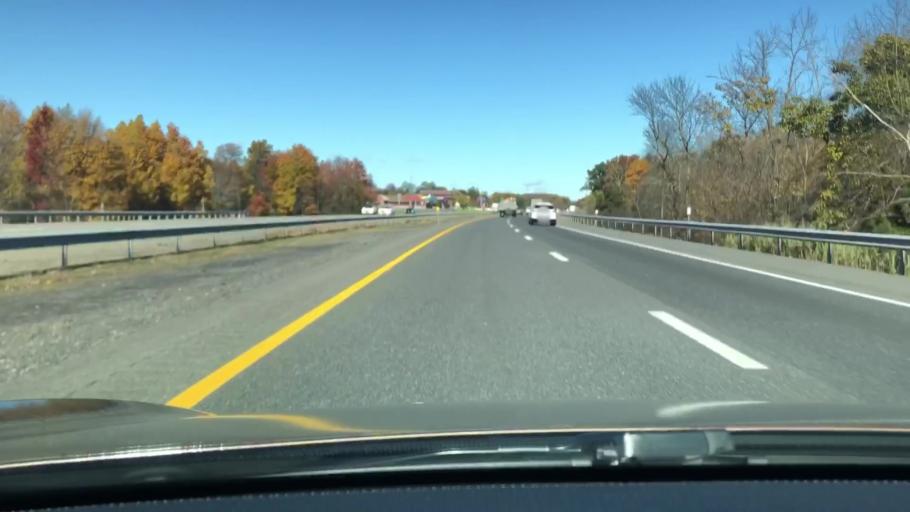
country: US
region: New York
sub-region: Ulster County
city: Plattekill
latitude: 41.5879
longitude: -74.0887
